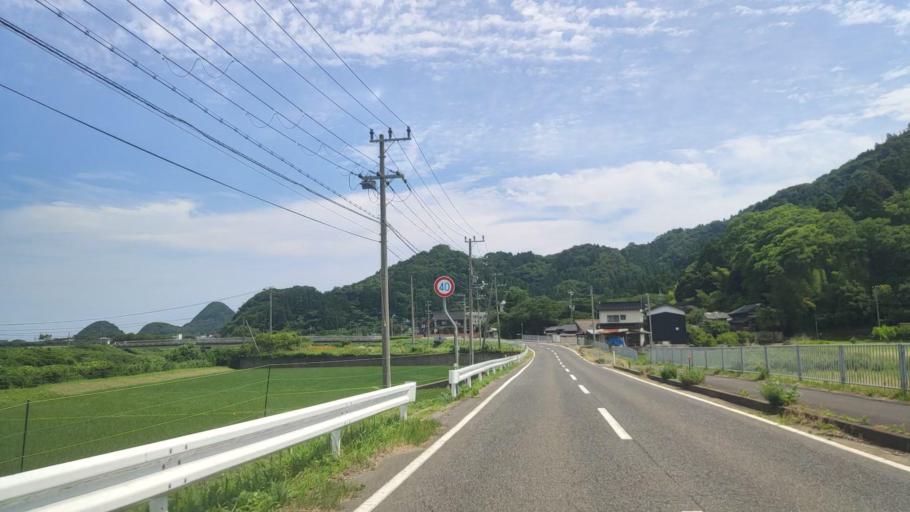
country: JP
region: Hyogo
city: Toyooka
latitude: 35.6464
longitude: 134.7630
